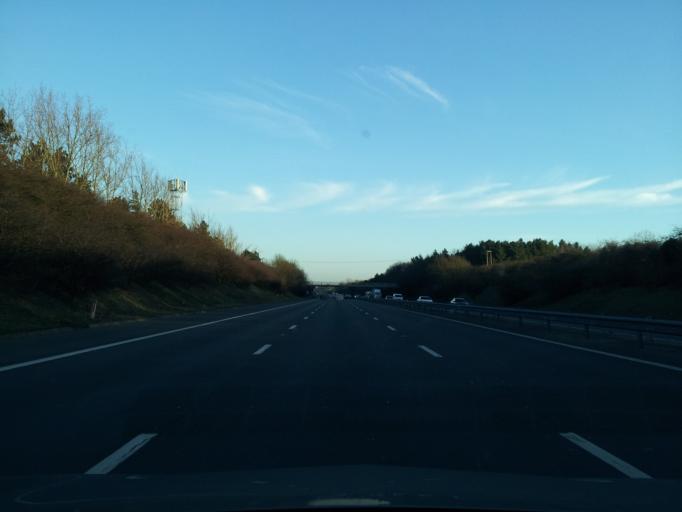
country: GB
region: England
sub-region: Milton Keynes
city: Newport Pagnell
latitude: 52.0784
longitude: -0.7400
